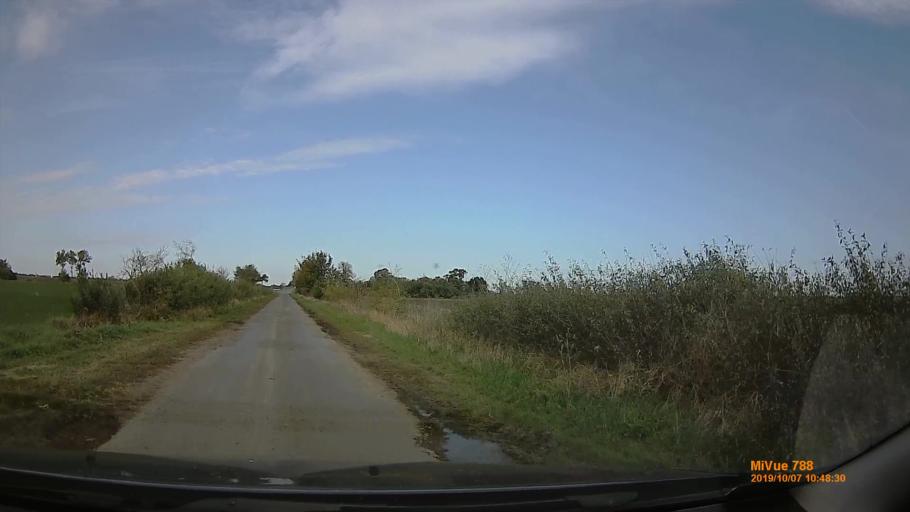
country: HU
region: Bekes
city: Kondoros
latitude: 46.7326
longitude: 20.8108
